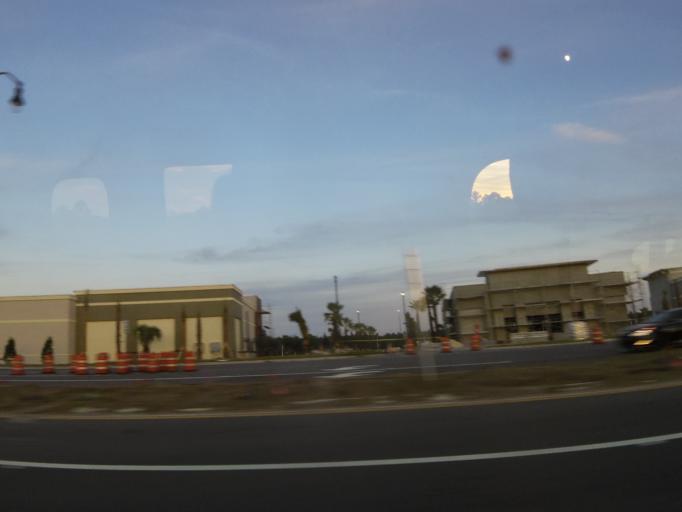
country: US
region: Florida
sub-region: Saint Johns County
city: Fruit Cove
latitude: 30.0979
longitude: -81.5226
